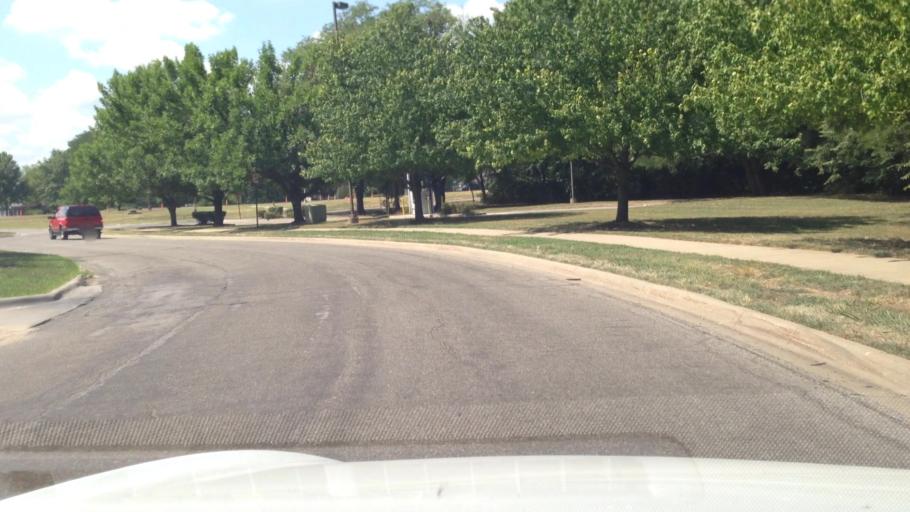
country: US
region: Kansas
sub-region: Douglas County
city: Lawrence
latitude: 38.9440
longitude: -95.2826
